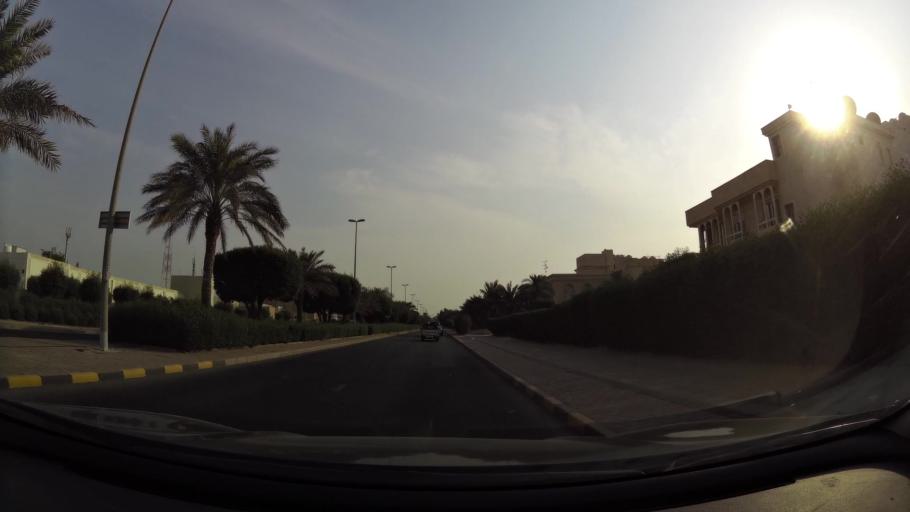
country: KW
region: Mubarak al Kabir
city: Mubarak al Kabir
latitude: 29.2027
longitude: 48.0690
